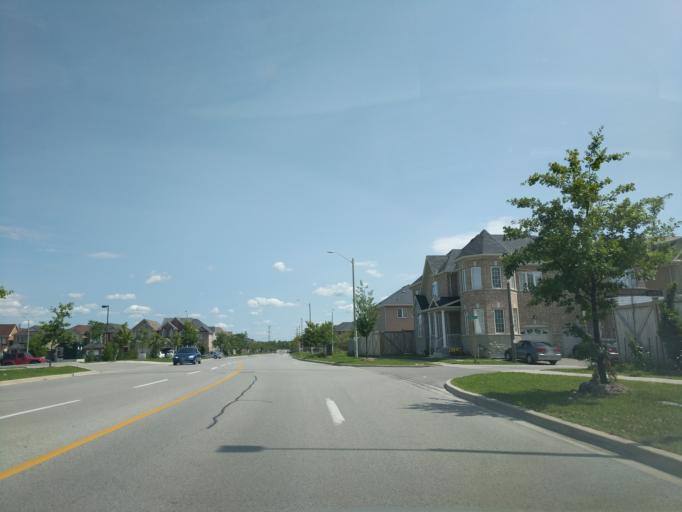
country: CA
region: Ontario
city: Markham
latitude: 43.8445
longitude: -79.2520
